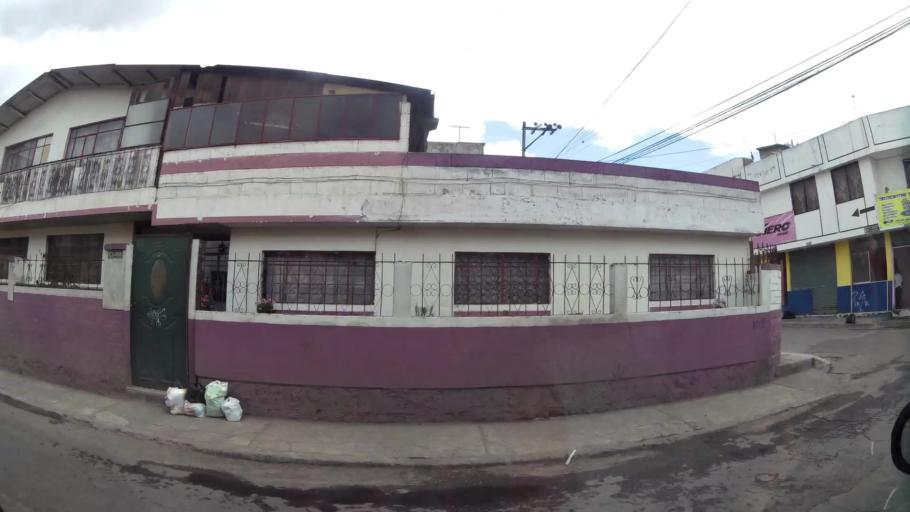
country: EC
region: Pichincha
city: Quito
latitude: -0.0833
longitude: -78.4184
